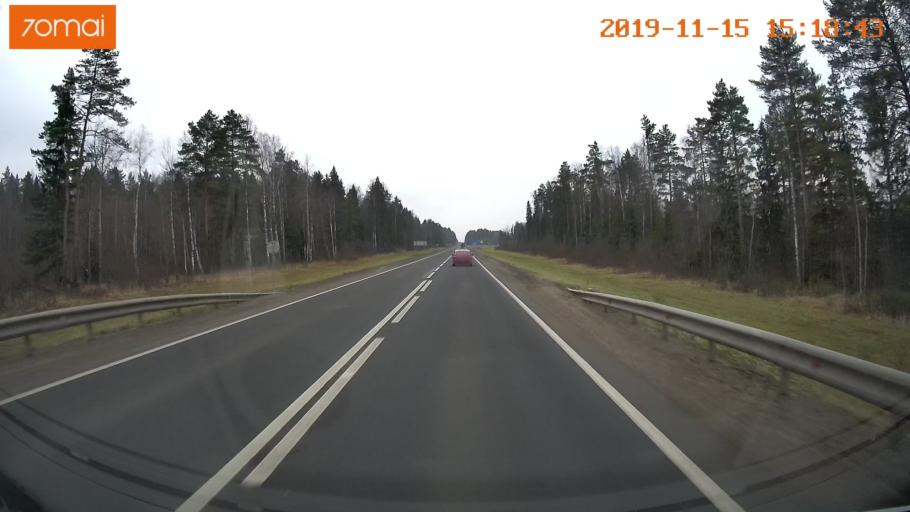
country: RU
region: Jaroslavl
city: Danilov
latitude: 58.2435
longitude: 40.1817
